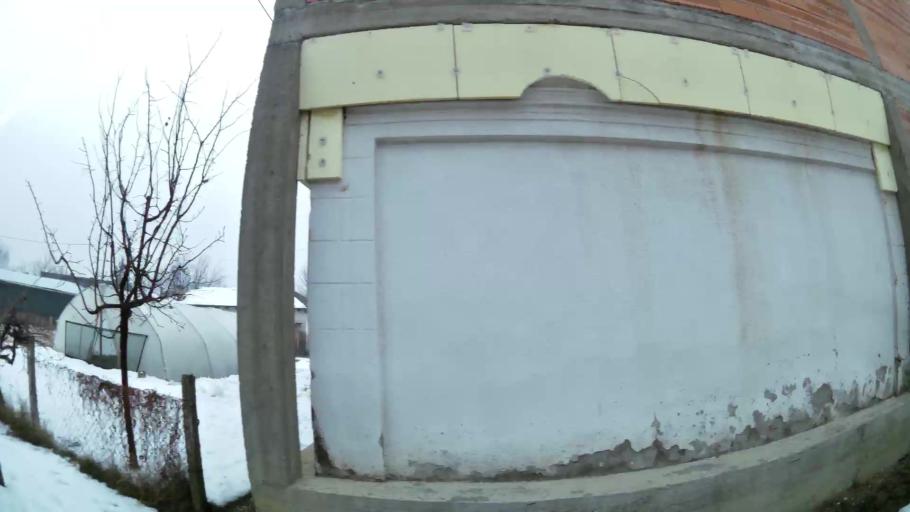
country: MK
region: Petrovec
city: Petrovec
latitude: 41.9395
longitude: 21.6174
